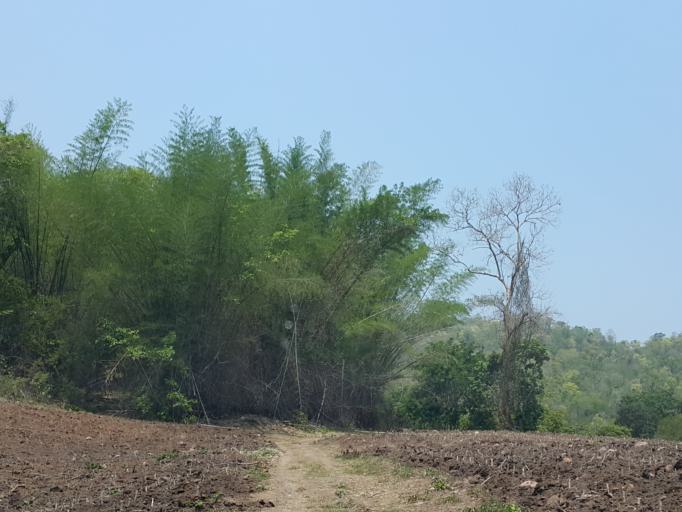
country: TH
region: Kanchanaburi
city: Sai Yok
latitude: 14.2147
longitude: 98.8757
